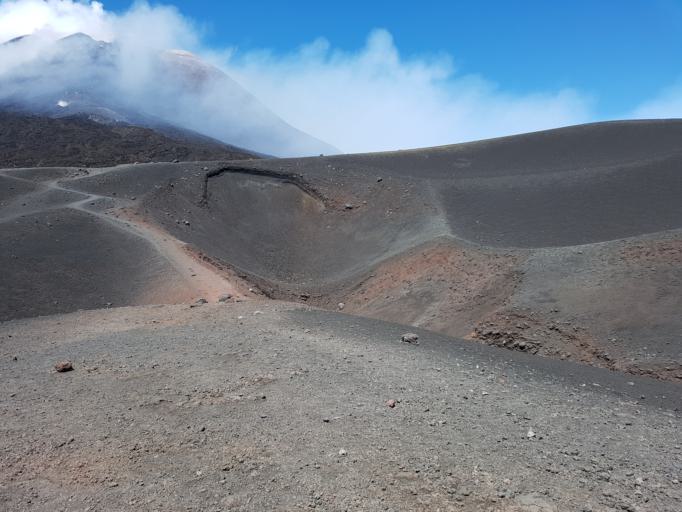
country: IT
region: Sicily
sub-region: Catania
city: Ragalna
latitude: 37.7344
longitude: 14.9997
